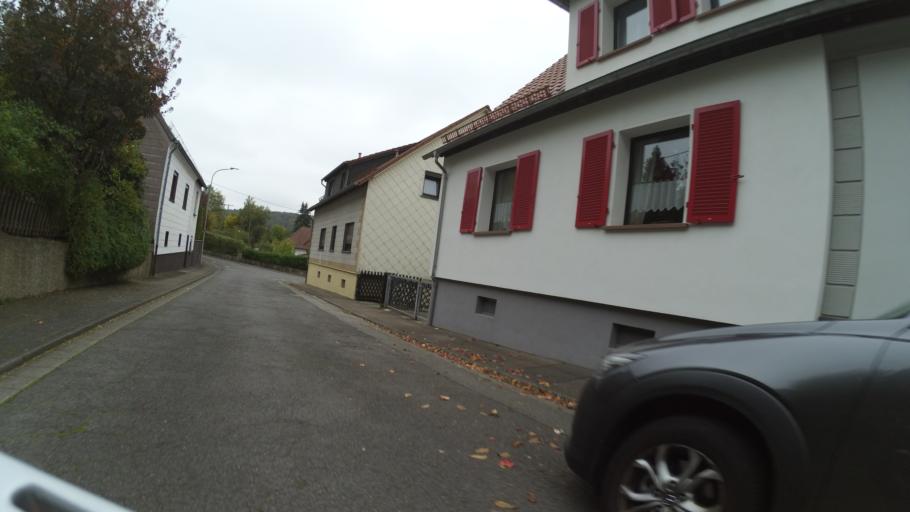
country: DE
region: Saarland
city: Blieskastel
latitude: 49.2644
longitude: 7.2823
